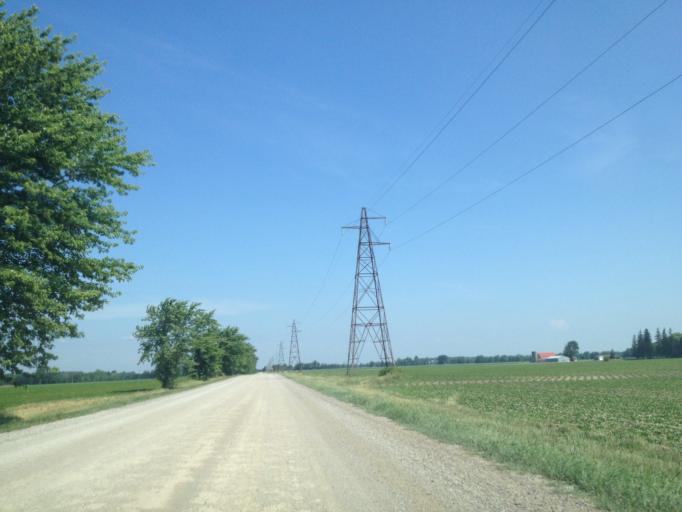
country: CA
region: Ontario
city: London
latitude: 43.1175
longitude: -81.2329
